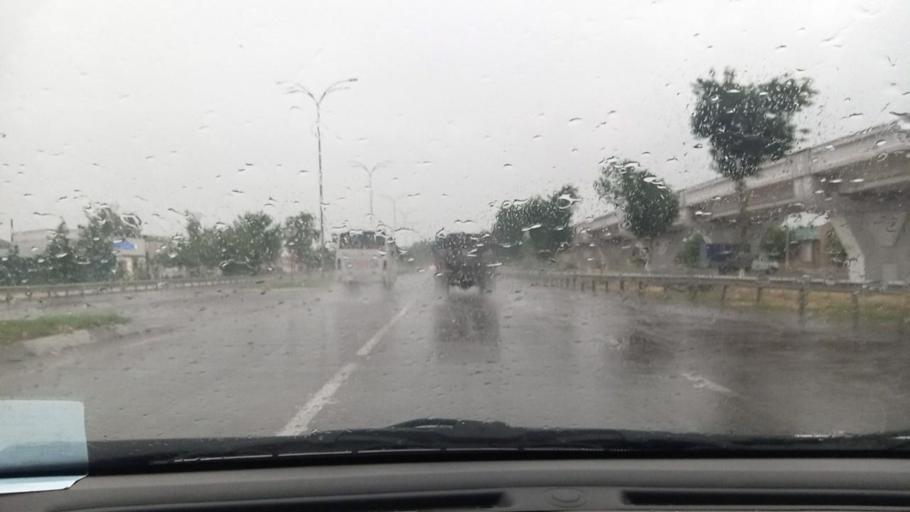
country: UZ
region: Toshkent Shahri
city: Bektemir
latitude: 41.2752
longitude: 69.3618
